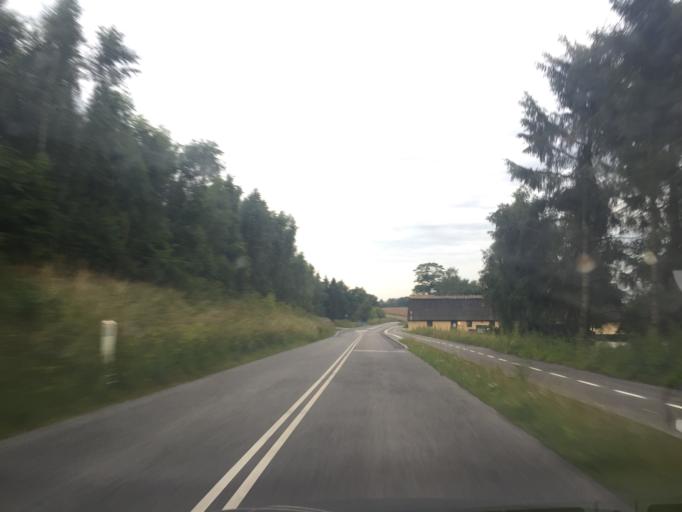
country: DK
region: Zealand
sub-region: Roskilde Kommune
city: Gundsomagle
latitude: 55.7497
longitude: 12.1392
